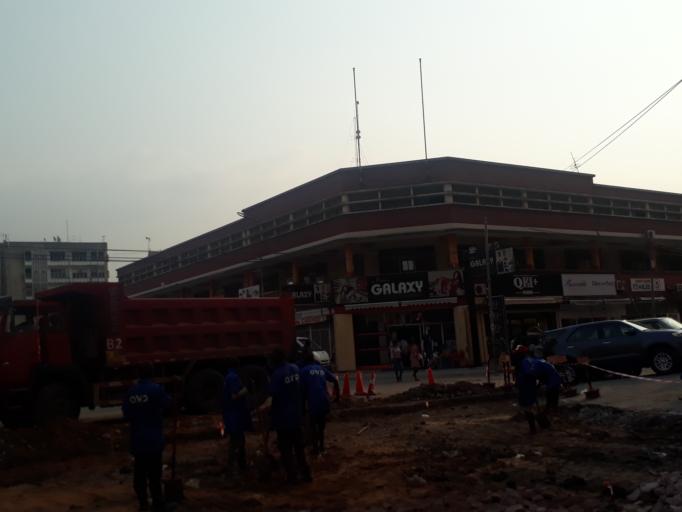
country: CD
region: Kinshasa
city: Kinshasa
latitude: -4.3016
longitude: 15.3107
